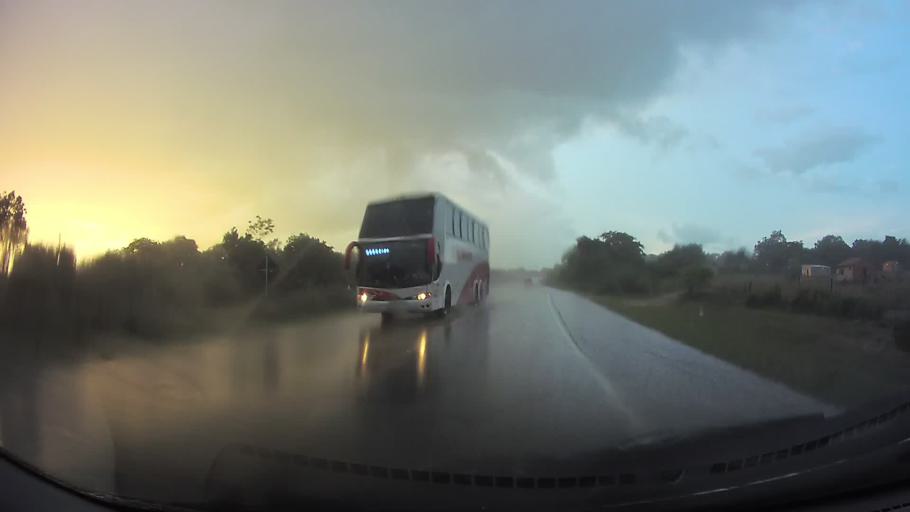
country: PY
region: Paraguari
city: Paraguari
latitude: -25.6281
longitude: -57.1613
